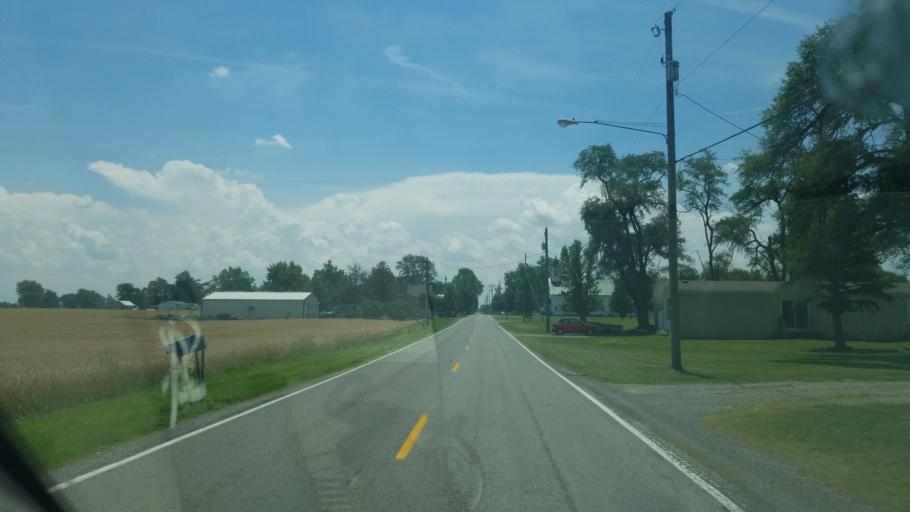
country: US
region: Ohio
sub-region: Hancock County
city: Arlington
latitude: 40.9382
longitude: -83.5944
